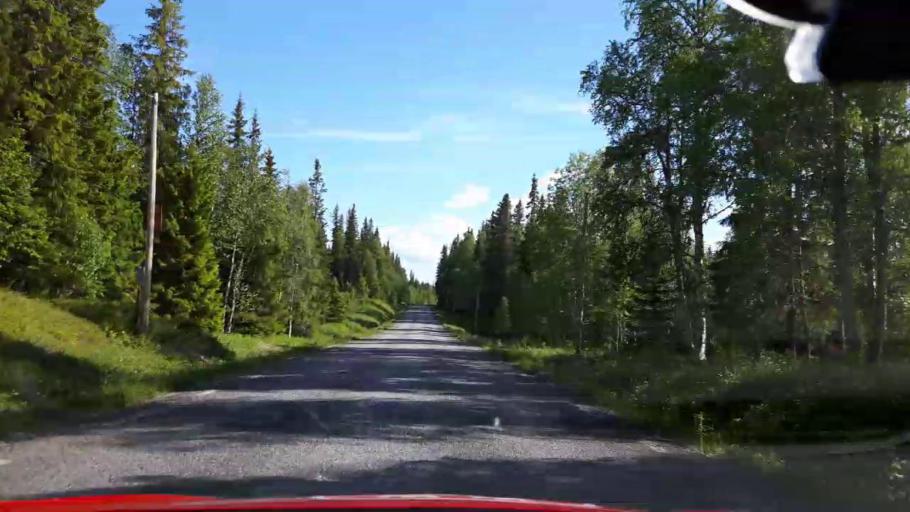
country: SE
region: Jaemtland
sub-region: Krokoms Kommun
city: Valla
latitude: 63.7479
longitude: 14.1177
